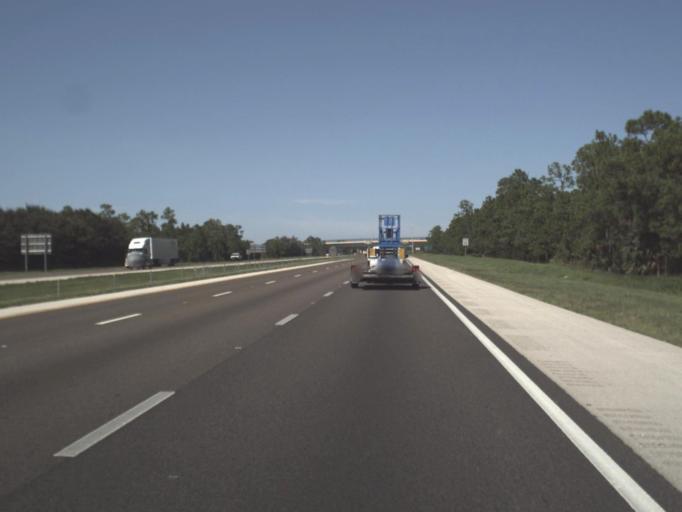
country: US
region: Florida
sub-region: Lee County
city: Estero
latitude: 26.4413
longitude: -81.7809
